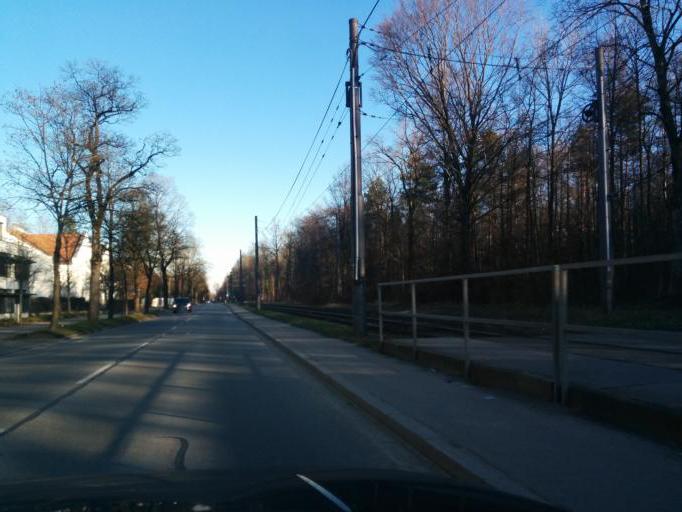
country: DE
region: Bavaria
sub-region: Upper Bavaria
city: Pullach im Isartal
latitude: 48.0771
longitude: 11.5501
